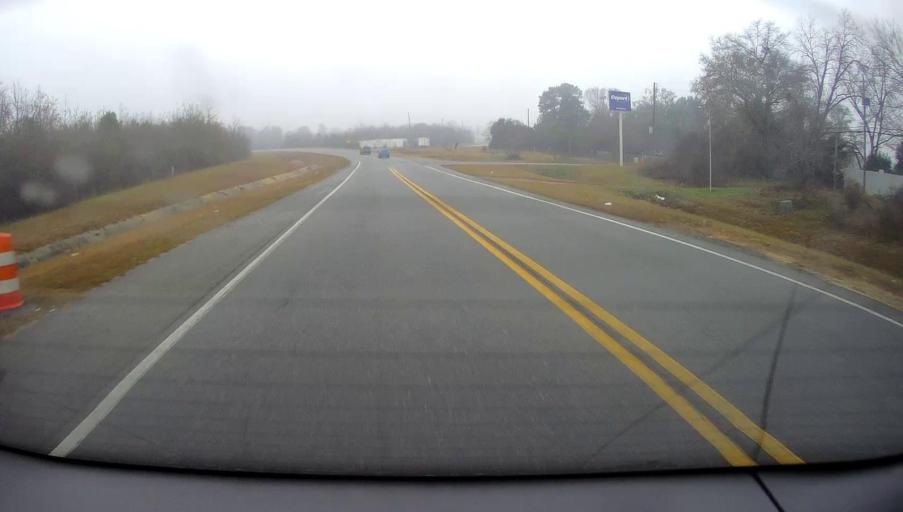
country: US
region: Georgia
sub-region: Houston County
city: Centerville
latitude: 32.6836
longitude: -83.7028
